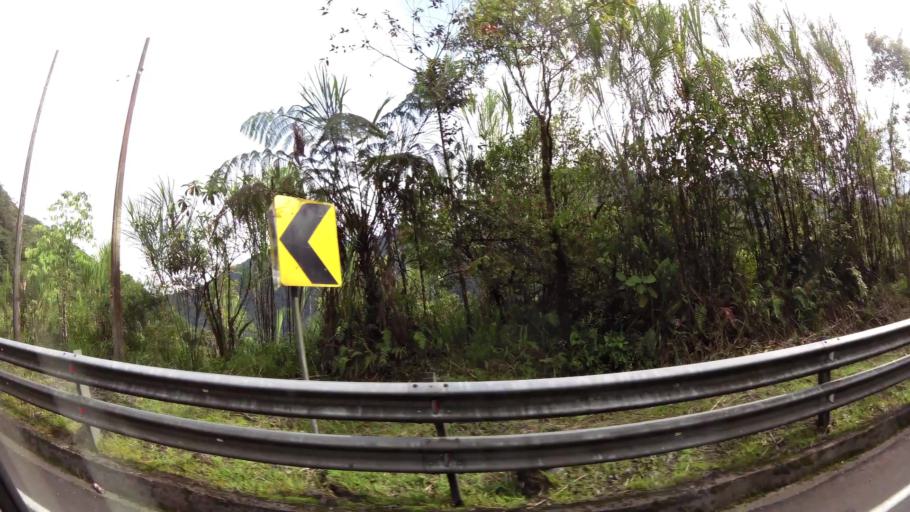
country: EC
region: Pastaza
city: Puyo
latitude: -1.4453
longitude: -78.1780
